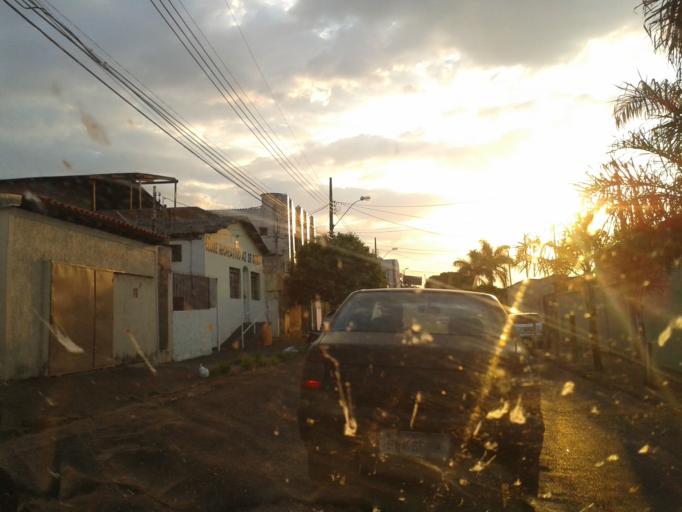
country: BR
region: Minas Gerais
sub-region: Uberlandia
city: Uberlandia
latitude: -18.9046
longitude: -48.2781
